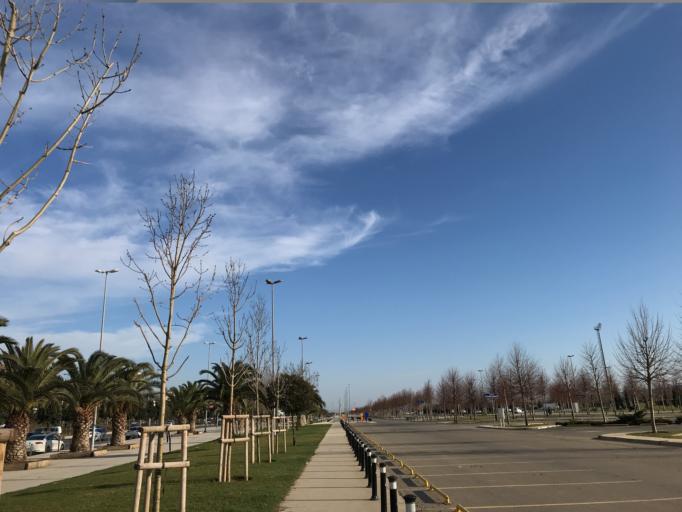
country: TR
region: Istanbul
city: Maltepe
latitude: 40.9315
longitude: 29.1179
